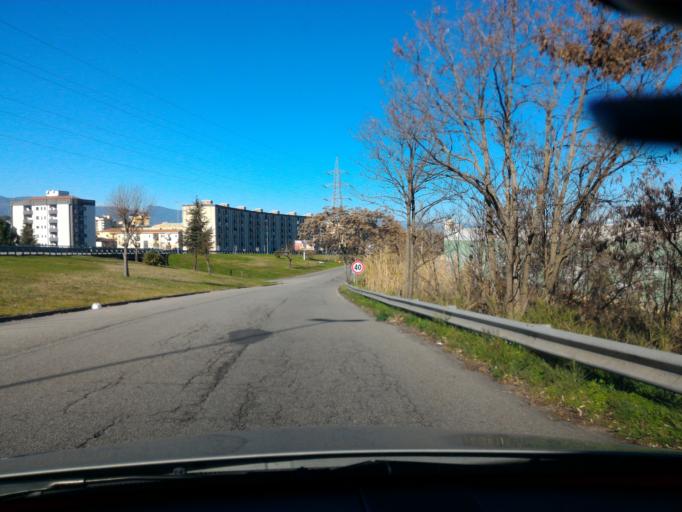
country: IT
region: Calabria
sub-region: Provincia di Cosenza
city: Cosenza
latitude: 39.3134
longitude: 16.2597
